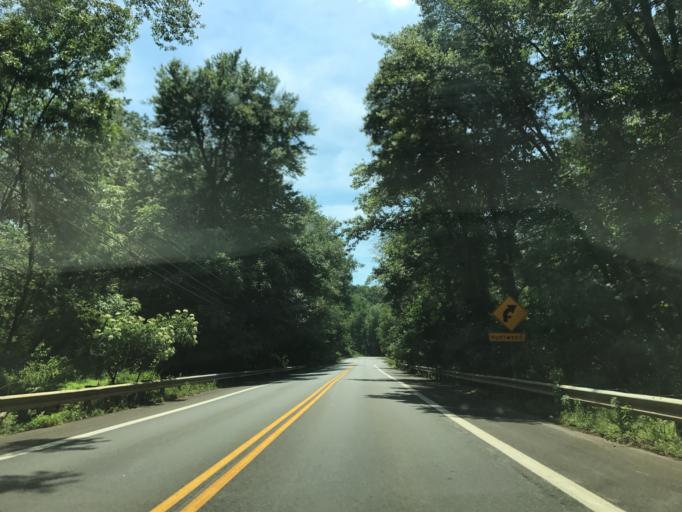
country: US
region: Maryland
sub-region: Anne Arundel County
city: Crownsville
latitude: 38.9908
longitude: -76.6367
